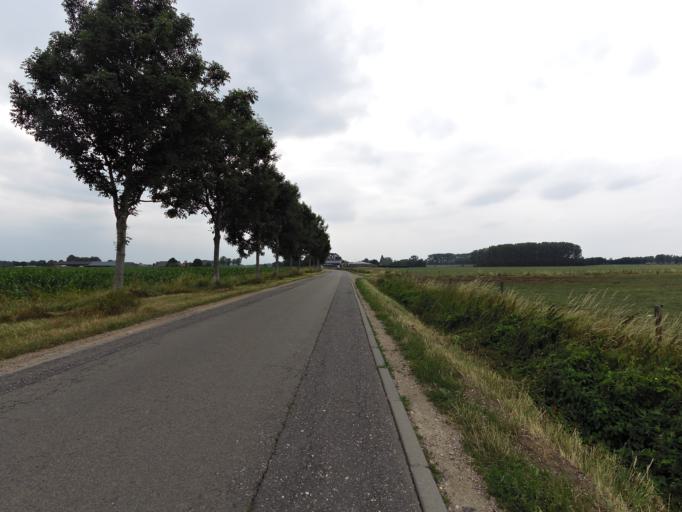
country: DE
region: North Rhine-Westphalia
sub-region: Regierungsbezirk Dusseldorf
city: Kranenburg
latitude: 51.8578
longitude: 6.0266
